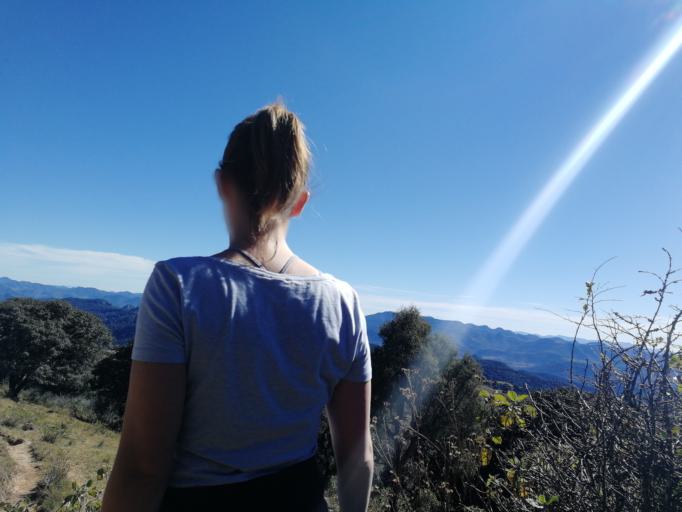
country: MX
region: San Luis Potosi
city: Zaragoza
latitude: 22.0073
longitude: -100.6156
